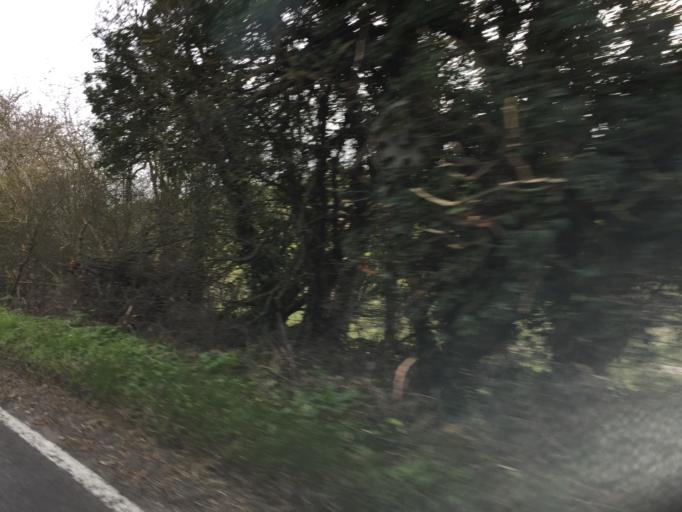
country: GB
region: England
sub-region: Oxfordshire
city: Cholsey
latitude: 51.5447
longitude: -1.1637
